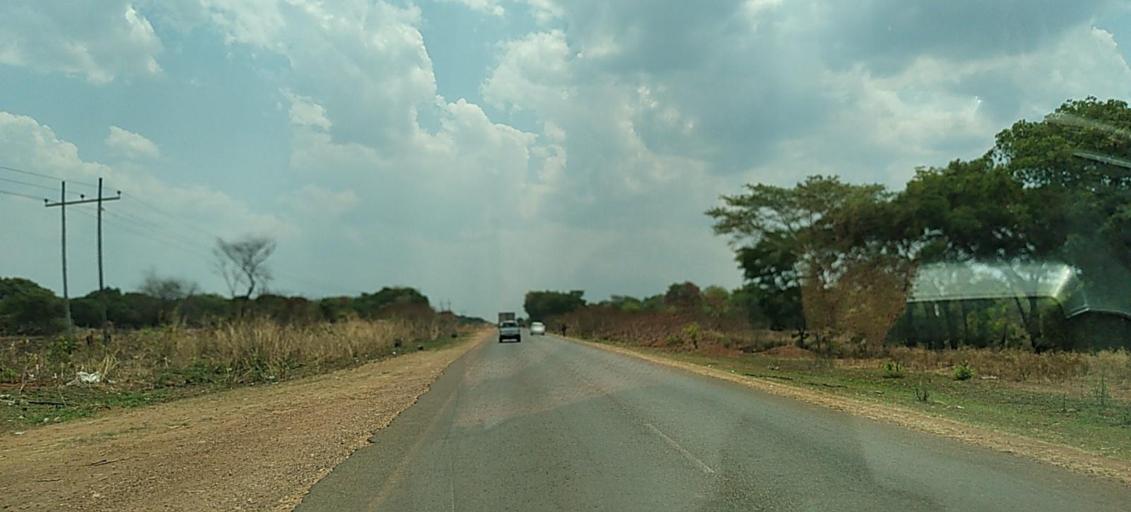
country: ZM
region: Copperbelt
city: Kalulushi
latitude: -12.8350
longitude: 27.9600
